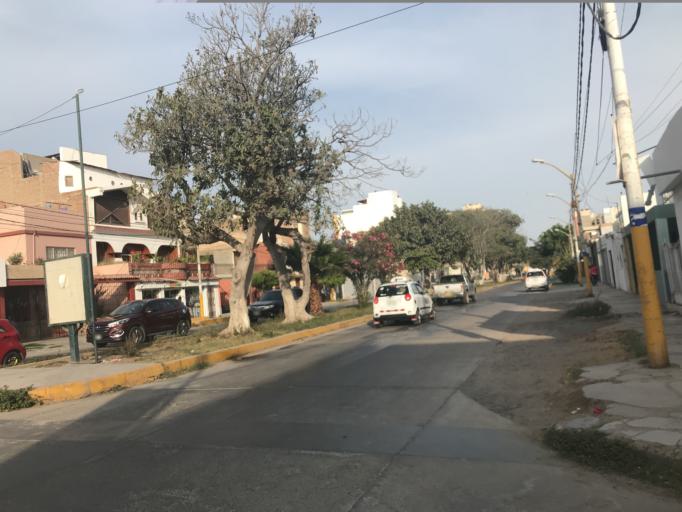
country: PE
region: Lambayeque
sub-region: Provincia de Chiclayo
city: Chiclayo
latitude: -6.7825
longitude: -79.8414
